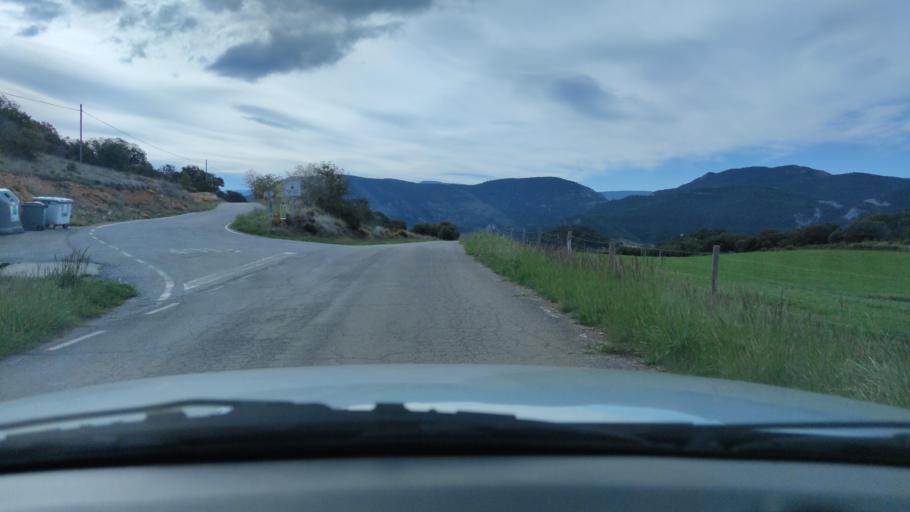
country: ES
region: Catalonia
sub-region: Provincia de Lleida
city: Coll de Nargo
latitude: 42.2386
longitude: 1.3803
